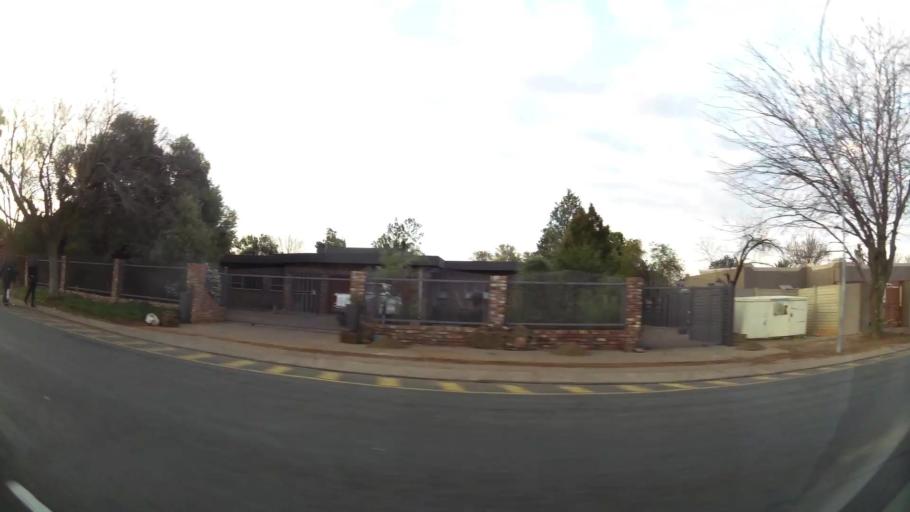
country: ZA
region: Orange Free State
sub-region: Mangaung Metropolitan Municipality
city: Bloemfontein
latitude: -29.1527
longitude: 26.1807
